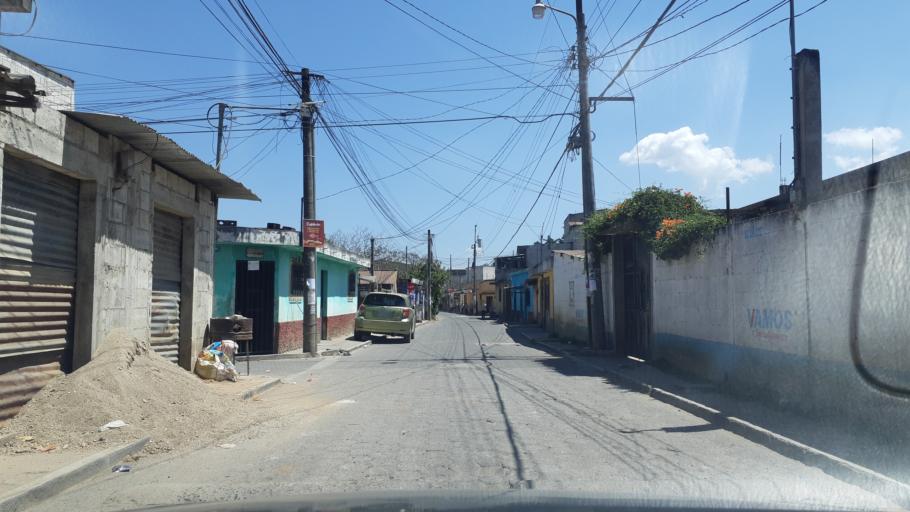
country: GT
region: Chimaltenango
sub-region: Municipio de Chimaltenango
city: Chimaltenango
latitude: 14.6524
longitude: -90.8130
